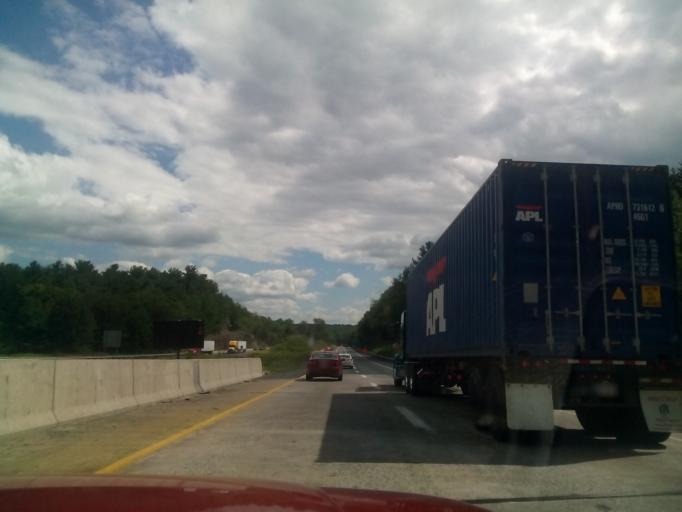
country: US
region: Pennsylvania
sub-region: Monroe County
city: Tannersville
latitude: 41.0228
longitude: -75.3053
